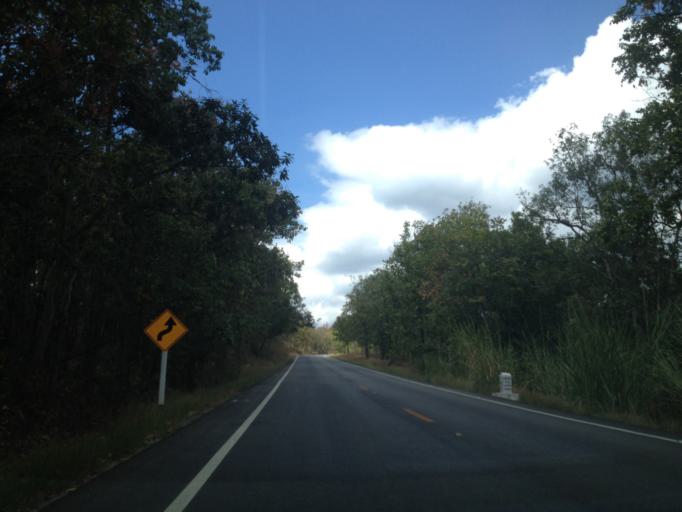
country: TH
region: Chiang Mai
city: Hot
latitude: 18.1528
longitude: 98.4147
